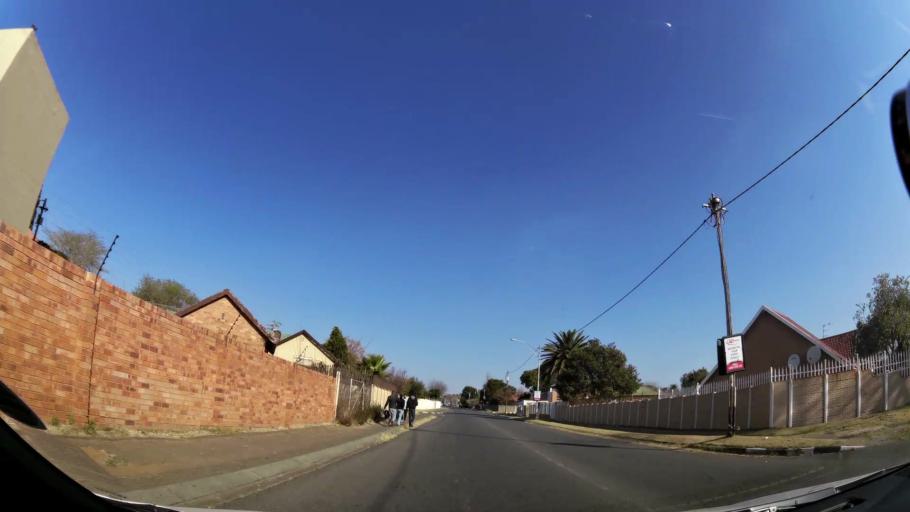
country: ZA
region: Gauteng
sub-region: City of Johannesburg Metropolitan Municipality
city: Johannesburg
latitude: -26.2373
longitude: 28.0211
